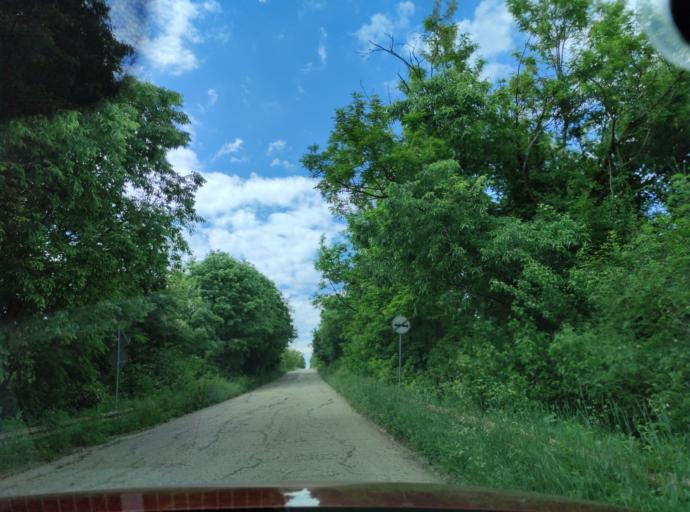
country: BG
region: Montana
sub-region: Obshtina Berkovitsa
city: Berkovitsa
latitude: 43.3559
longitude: 23.0951
